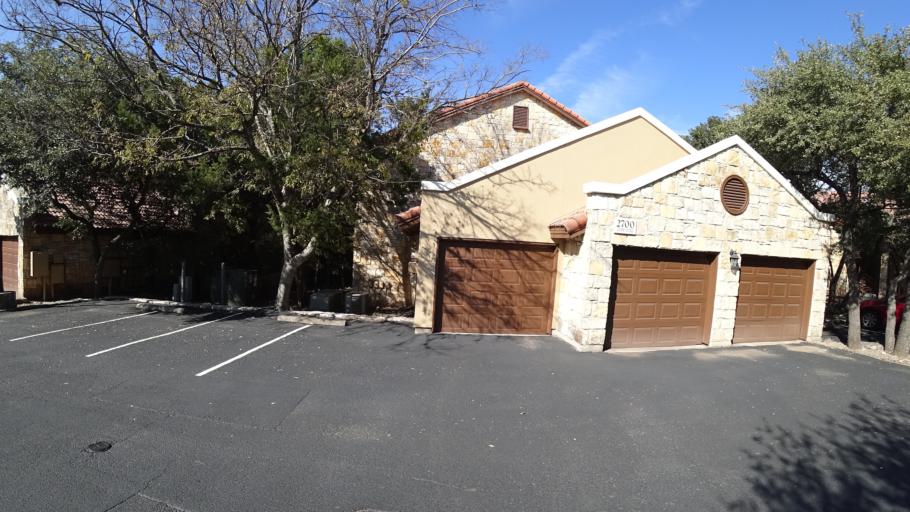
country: US
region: Texas
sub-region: Williamson County
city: Jollyville
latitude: 30.3737
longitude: -97.7620
